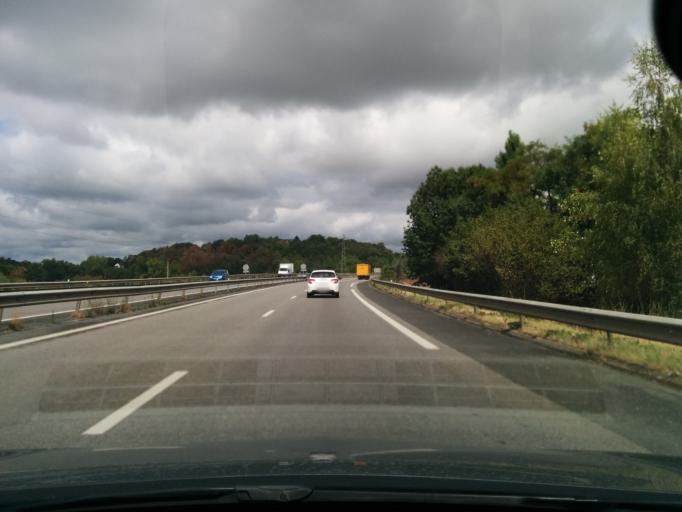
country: FR
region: Limousin
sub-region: Departement de la Correze
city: Saint-Pantaleon-de-Larche
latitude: 45.1601
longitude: 1.4802
